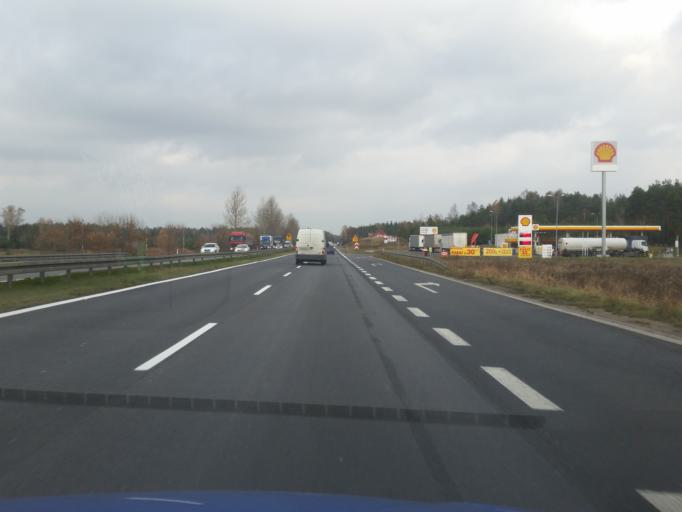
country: PL
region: Silesian Voivodeship
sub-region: Powiat bedzinski
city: Siewierz
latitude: 50.5112
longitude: 19.1958
